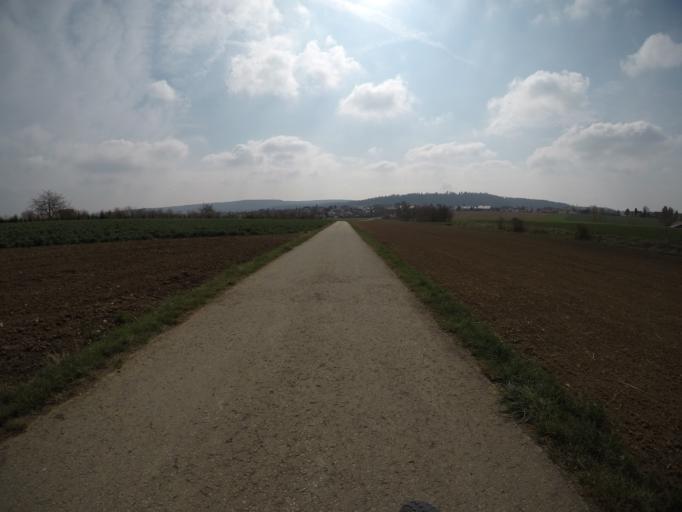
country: DE
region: Baden-Wuerttemberg
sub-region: Regierungsbezirk Stuttgart
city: Nufringen
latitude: 48.6288
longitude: 8.8840
